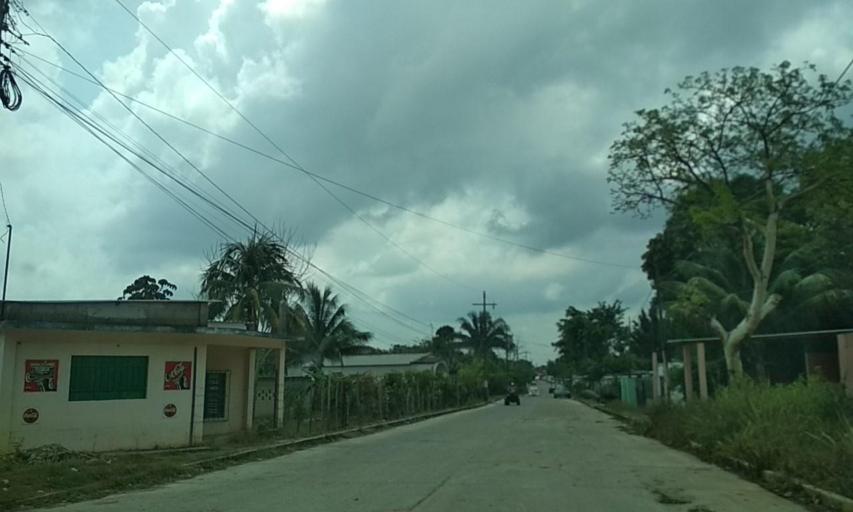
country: MX
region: Veracruz
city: Las Choapas
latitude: 17.9014
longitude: -94.1051
